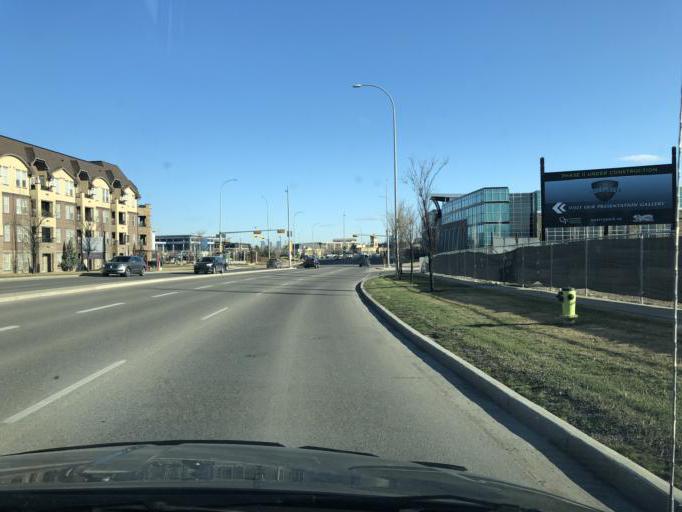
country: CA
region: Alberta
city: Calgary
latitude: 50.9584
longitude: -114.0089
